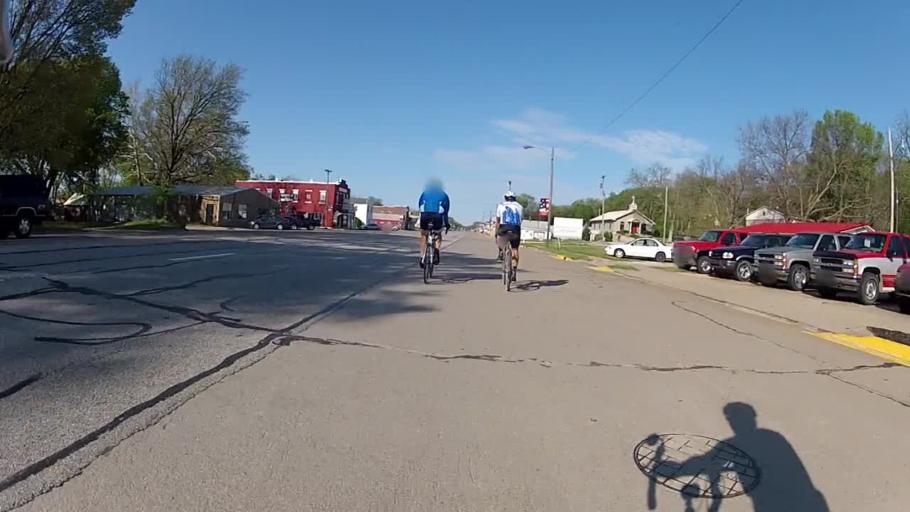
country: US
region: Kansas
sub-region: Riley County
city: Ogden
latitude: 39.1172
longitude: -96.7080
